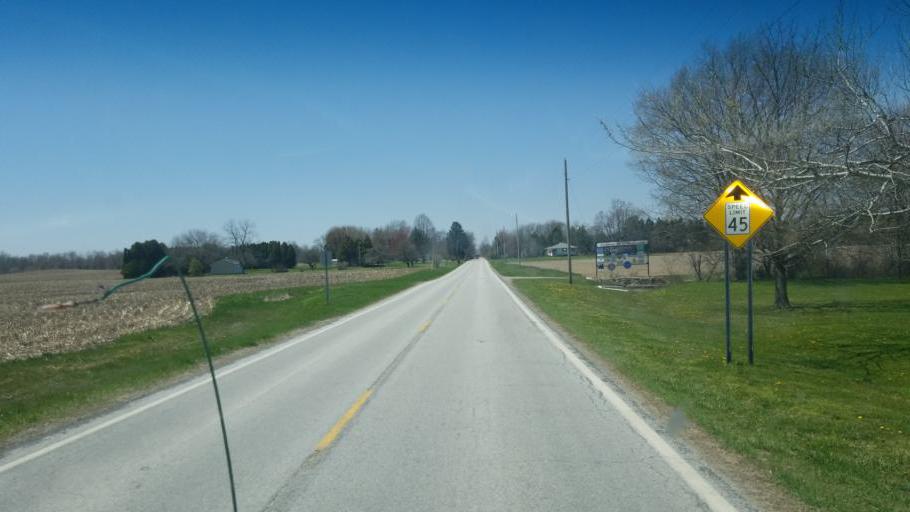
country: US
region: Ohio
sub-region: Huron County
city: New London
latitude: 41.0837
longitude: -82.3776
